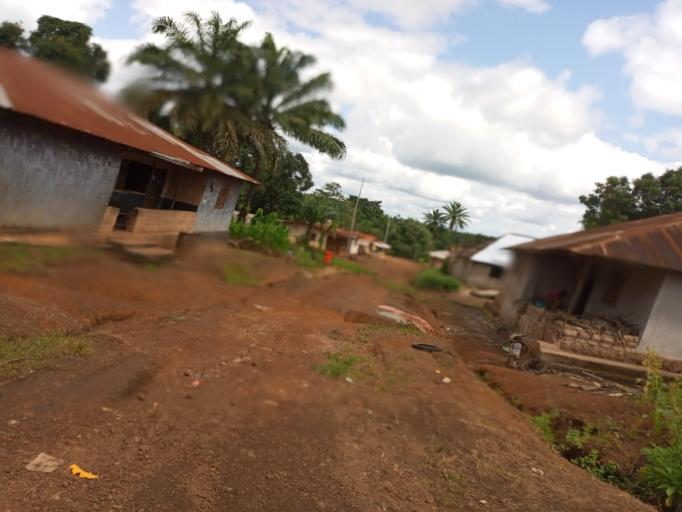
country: SL
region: Northern Province
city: Kamakwie
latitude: 9.4970
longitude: -12.2347
